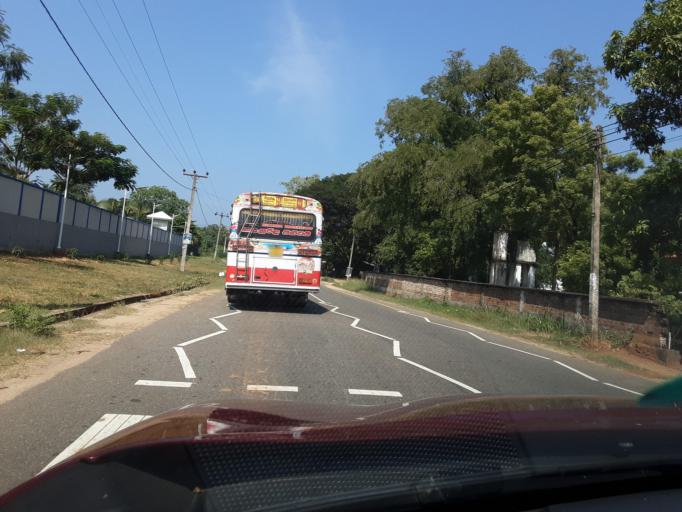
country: LK
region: Uva
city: Badulla
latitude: 7.1862
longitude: 81.0408
